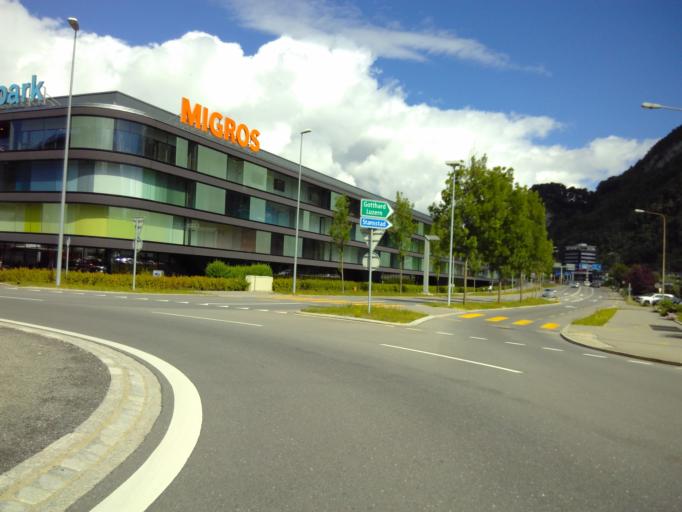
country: CH
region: Nidwalden
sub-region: Nidwalden
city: Stans
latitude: 46.9644
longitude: 8.3568
